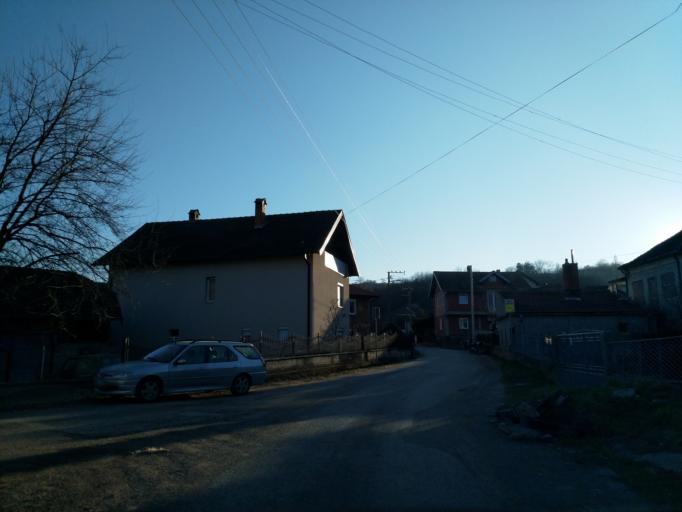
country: RS
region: Central Serbia
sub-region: Pomoravski Okrug
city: Paracin
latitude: 43.9343
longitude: 21.5199
